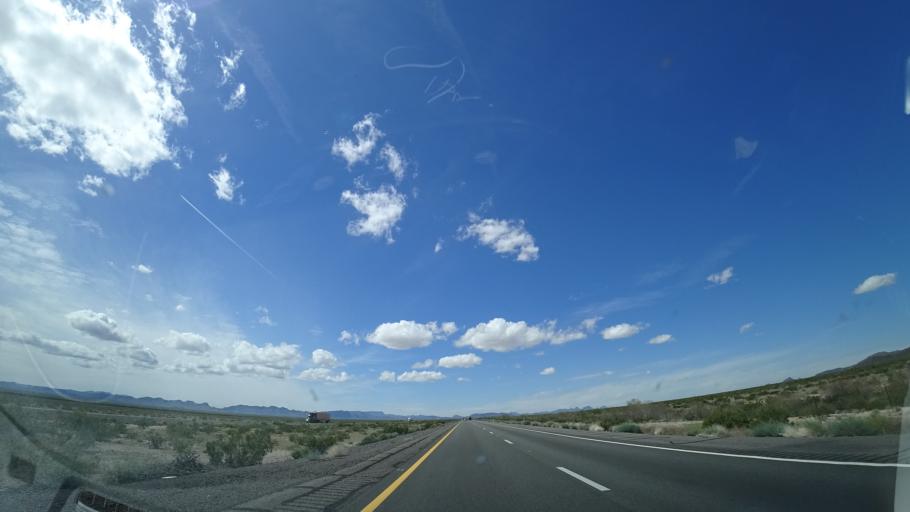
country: US
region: Arizona
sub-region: La Paz County
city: Salome
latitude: 33.6168
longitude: -113.6689
